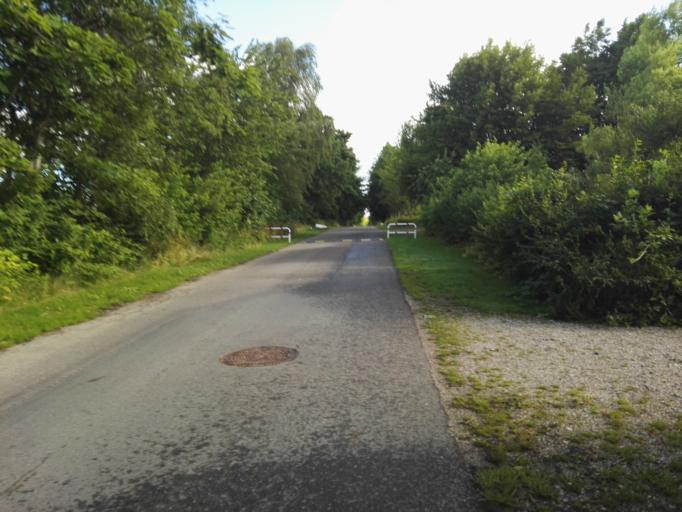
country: DK
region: Capital Region
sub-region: Ballerup Kommune
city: Ballerup
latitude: 55.7145
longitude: 12.3401
